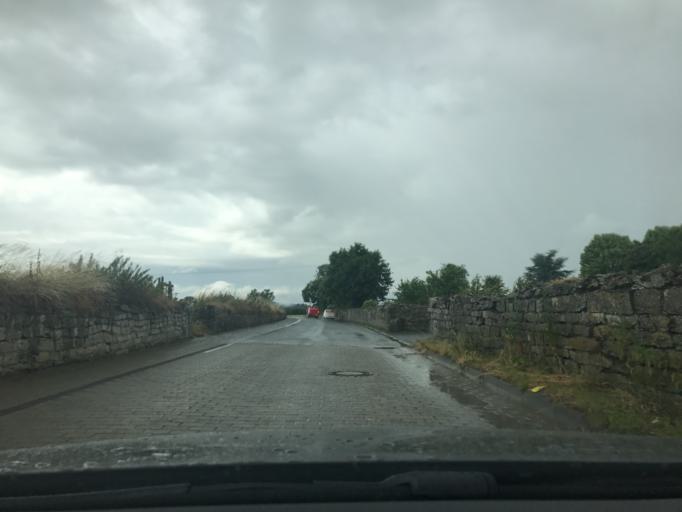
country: DE
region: North Rhine-Westphalia
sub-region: Regierungsbezirk Arnsberg
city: Anrochte
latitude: 51.5723
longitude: 8.2851
